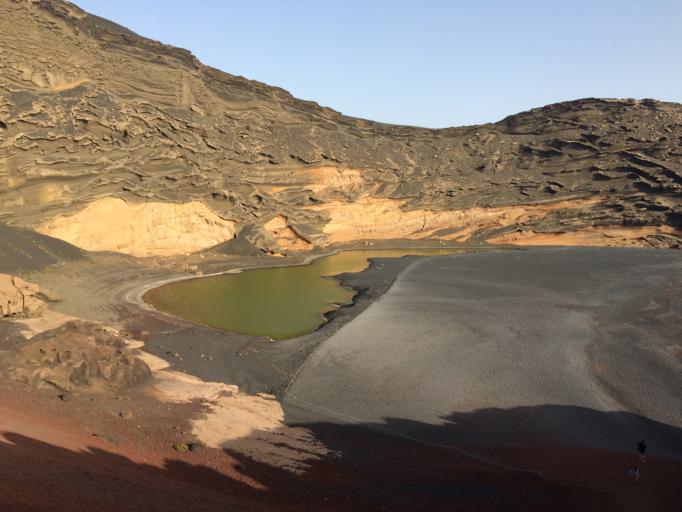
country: ES
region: Canary Islands
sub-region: Provincia de Las Palmas
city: Yaiza
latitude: 28.9783
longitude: -13.8286
